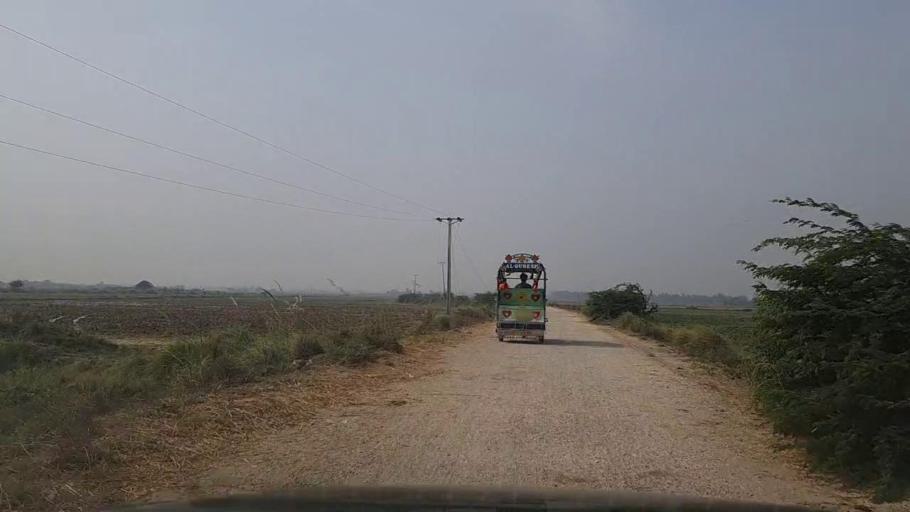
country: PK
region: Sindh
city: Mirpur Sakro
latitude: 24.5473
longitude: 67.8313
